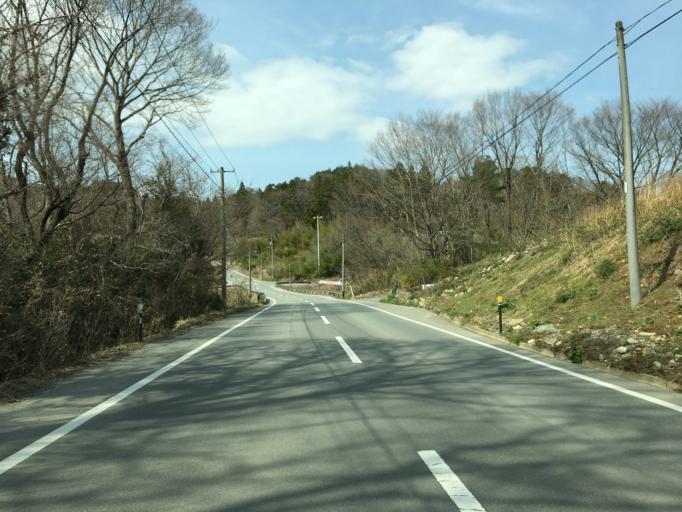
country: JP
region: Fukushima
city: Namie
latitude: 37.4563
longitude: 140.9737
